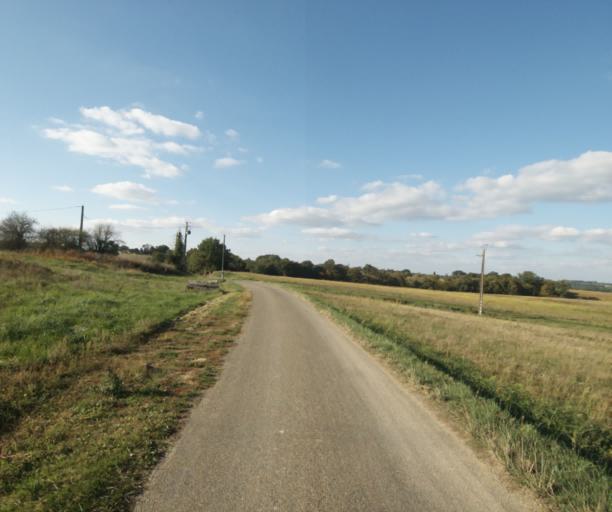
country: FR
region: Midi-Pyrenees
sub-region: Departement du Gers
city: Eauze
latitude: 43.7824
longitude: 0.1517
